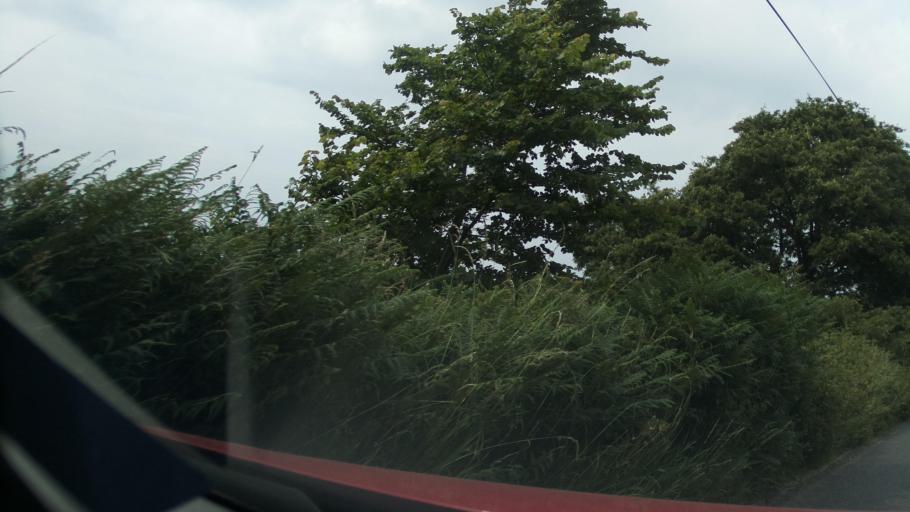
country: GB
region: England
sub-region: Devon
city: Colyton
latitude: 50.7187
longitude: -3.0523
